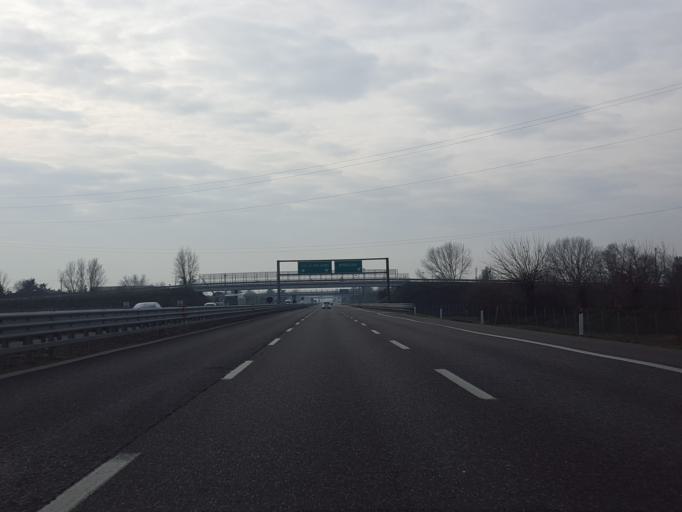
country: IT
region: Veneto
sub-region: Provincia di Vicenza
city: Brendola
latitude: 45.4940
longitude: 11.4460
